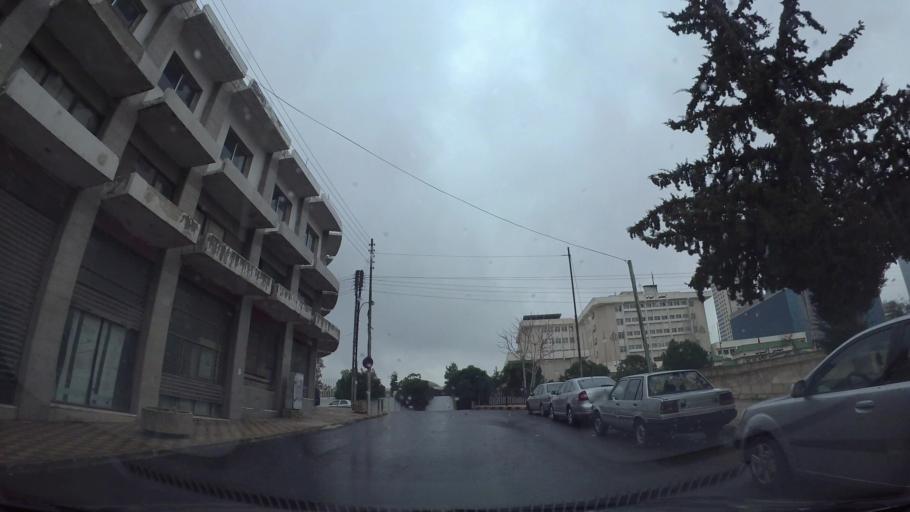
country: JO
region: Amman
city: Amman
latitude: 31.9643
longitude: 35.9132
